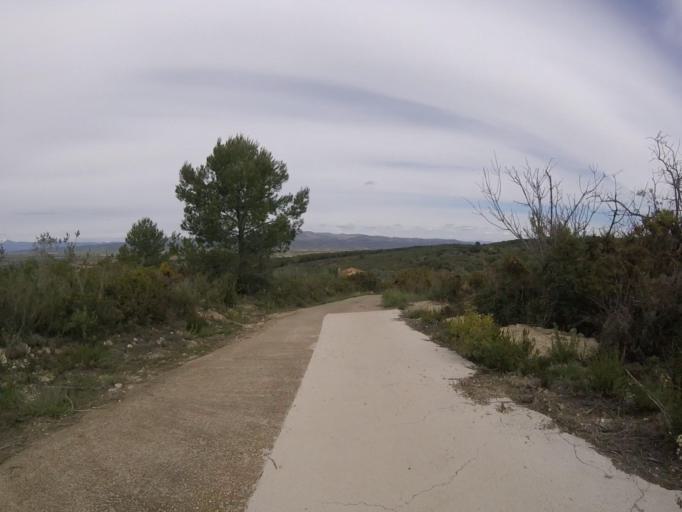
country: ES
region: Valencia
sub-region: Provincia de Castello
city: Cabanes
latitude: 40.1924
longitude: 0.0762
